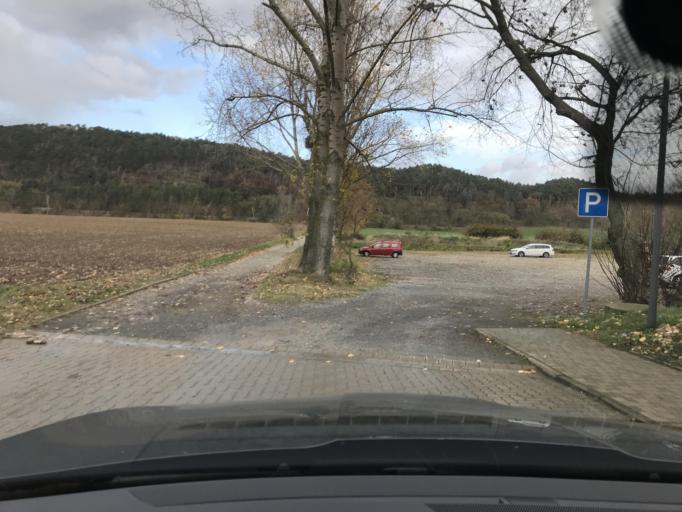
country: DE
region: Saxony-Anhalt
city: Langenstein
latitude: 51.8445
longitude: 11.0230
